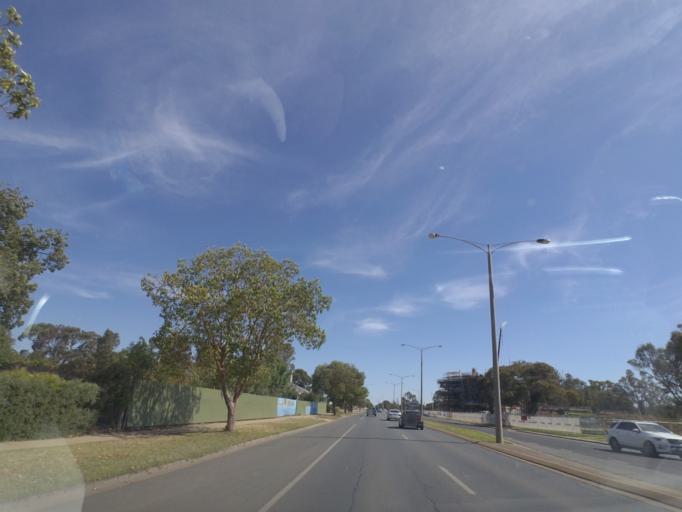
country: AU
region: Victoria
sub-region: Greater Shepparton
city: Shepparton
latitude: -36.3896
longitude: 145.3976
